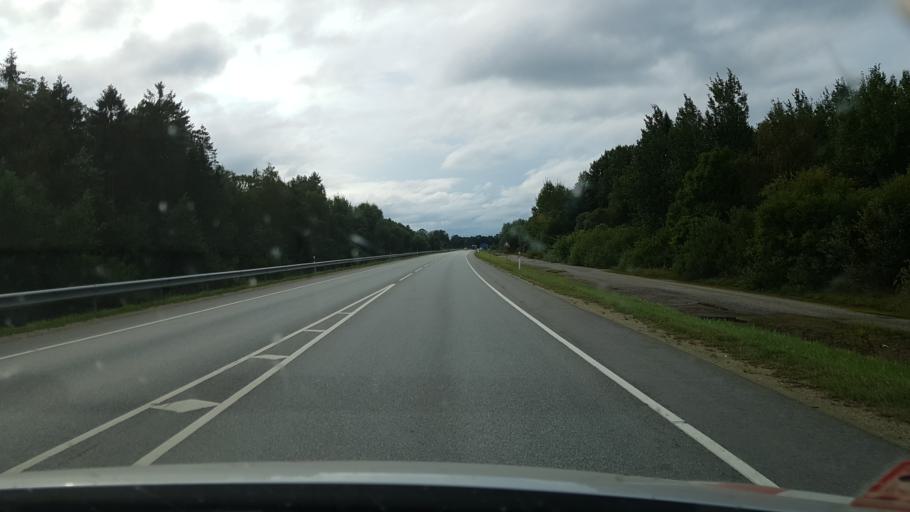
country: EE
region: Jogevamaa
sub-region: Poltsamaa linn
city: Poltsamaa
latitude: 58.6710
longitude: 25.9476
